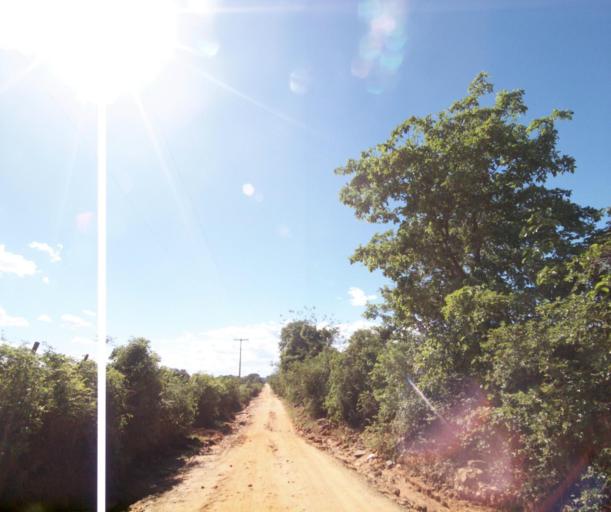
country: BR
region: Bahia
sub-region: Carinhanha
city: Carinhanha
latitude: -14.1861
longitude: -44.4964
